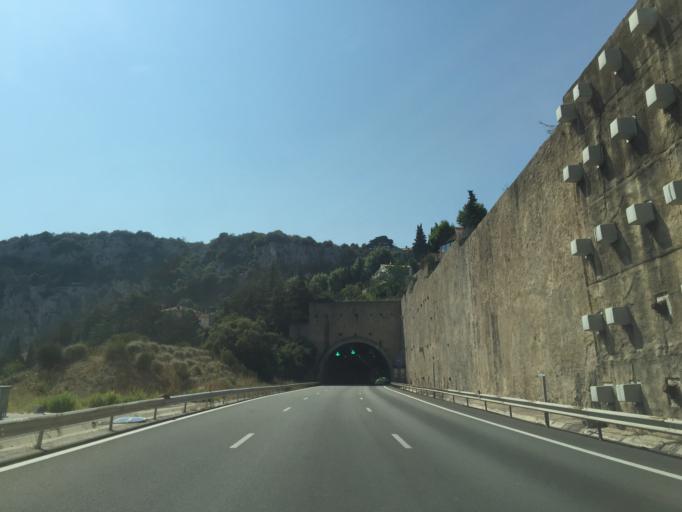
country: FR
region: Provence-Alpes-Cote d'Azur
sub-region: Departement des Alpes-Maritimes
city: La Turbie
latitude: 43.7519
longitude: 7.4060
